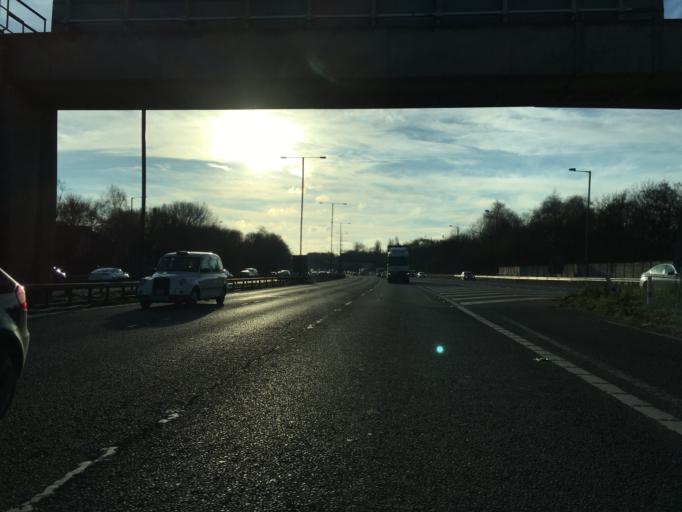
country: GB
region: England
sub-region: Manchester
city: Chorlton cum Hardy
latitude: 53.3933
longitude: -2.2712
